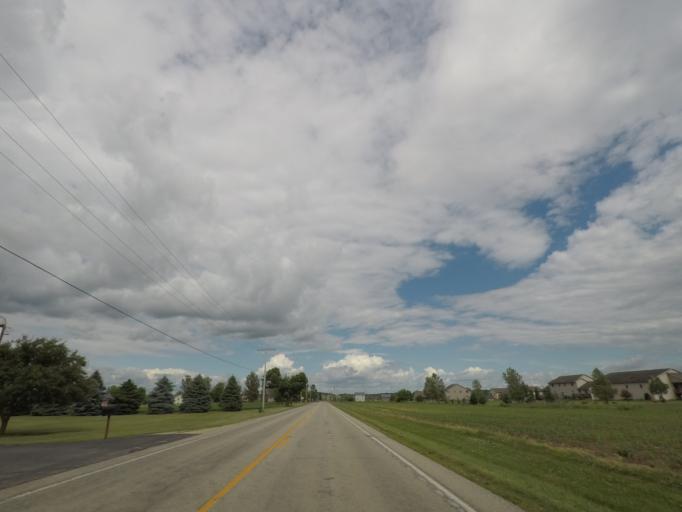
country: US
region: Wisconsin
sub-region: Dane County
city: Belleville
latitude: 42.8280
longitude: -89.4998
